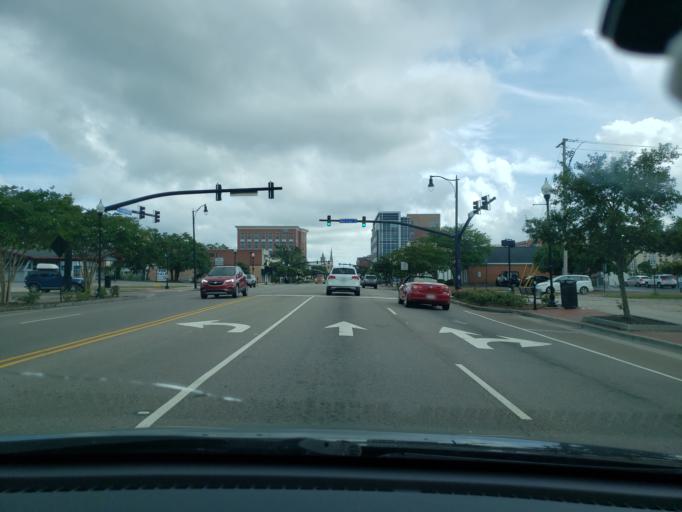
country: US
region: North Carolina
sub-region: New Hanover County
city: Wilmington
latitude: 34.2416
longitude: -77.9468
